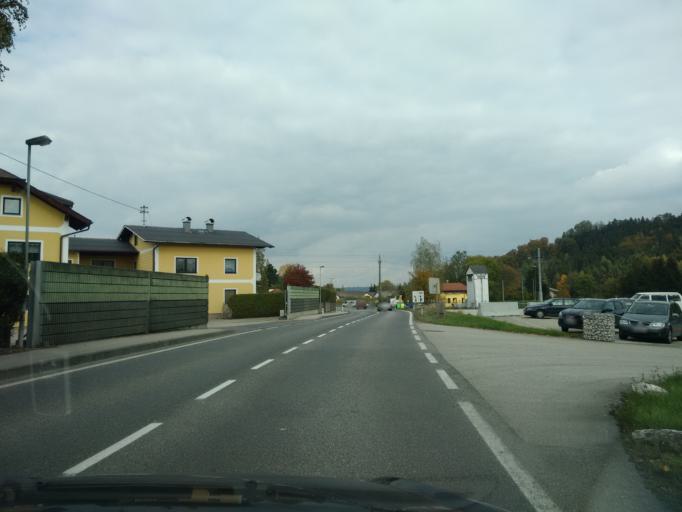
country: AT
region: Upper Austria
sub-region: Politischer Bezirk Vocklabruck
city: Lenzing
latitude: 47.9849
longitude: 13.6142
